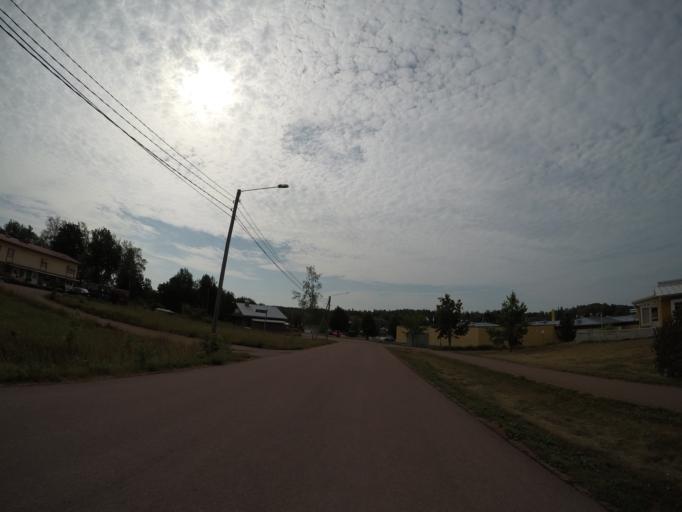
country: AX
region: Alands landsbygd
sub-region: Finstroem
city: Finstroem
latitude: 60.2317
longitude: 19.9890
